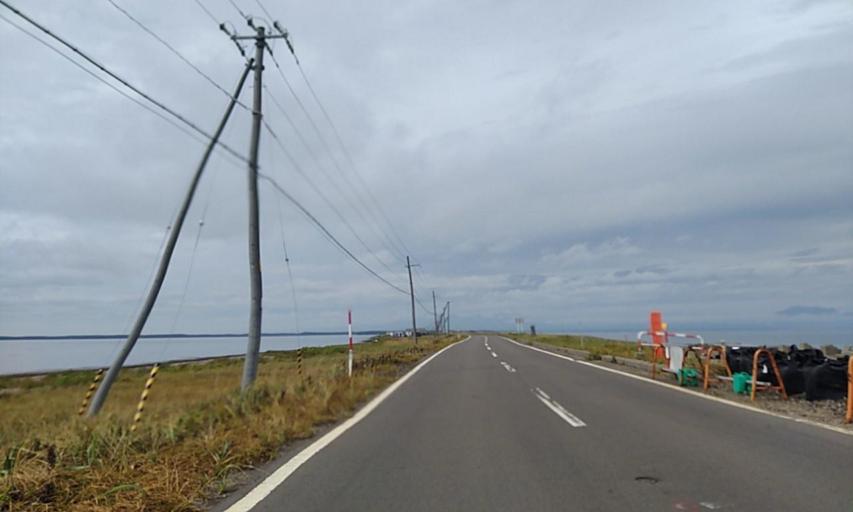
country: JP
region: Hokkaido
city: Shibetsu
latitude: 43.6113
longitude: 145.2647
